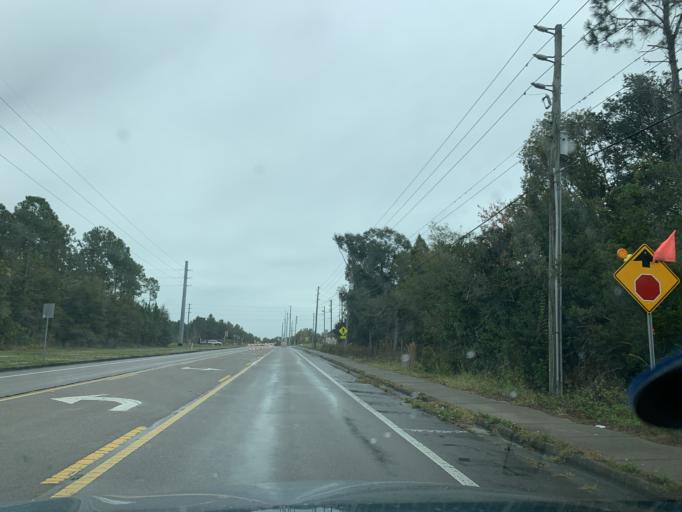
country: US
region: Florida
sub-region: Pasco County
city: Wesley Chapel
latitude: 28.2715
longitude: -82.3202
